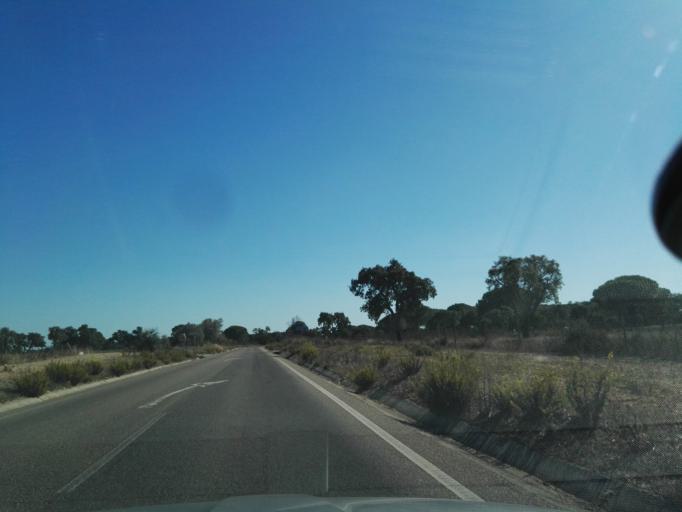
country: PT
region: Santarem
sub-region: Benavente
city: Poceirao
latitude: 38.8817
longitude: -8.7444
